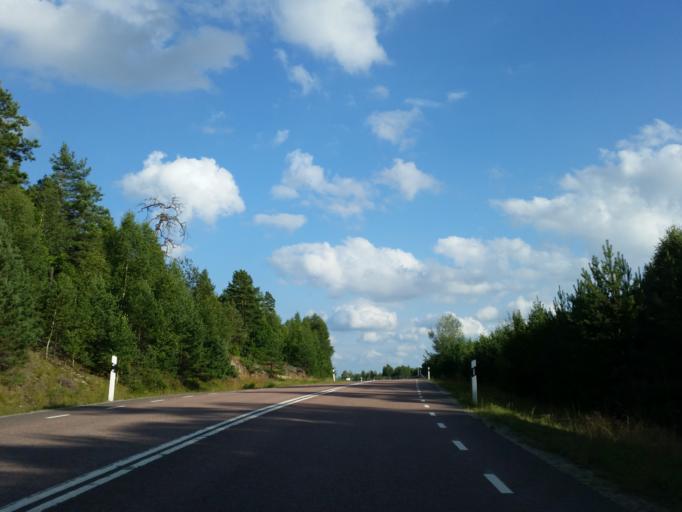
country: SE
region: Stockholm
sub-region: Nykvarns Kommun
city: Nykvarn
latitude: 59.2104
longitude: 17.3357
